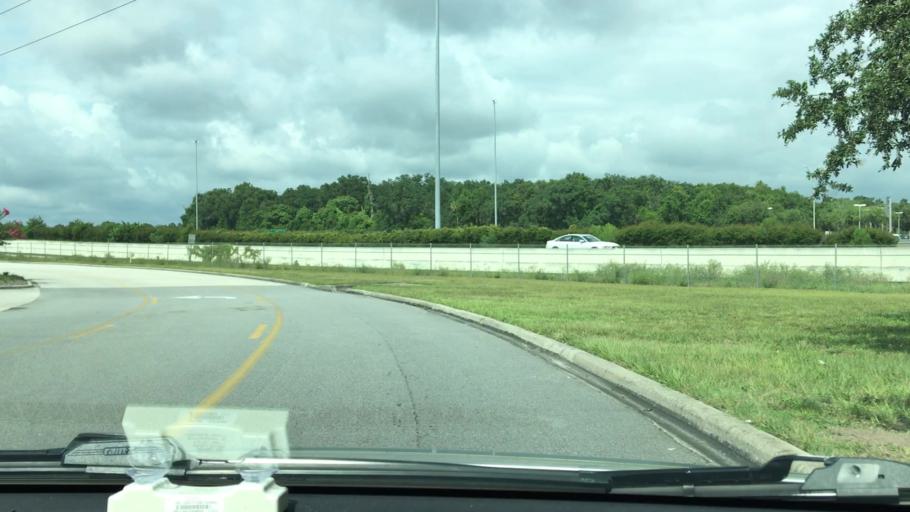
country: US
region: Florida
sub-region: Seminole County
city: Lake Mary
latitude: 28.8070
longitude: -81.3390
